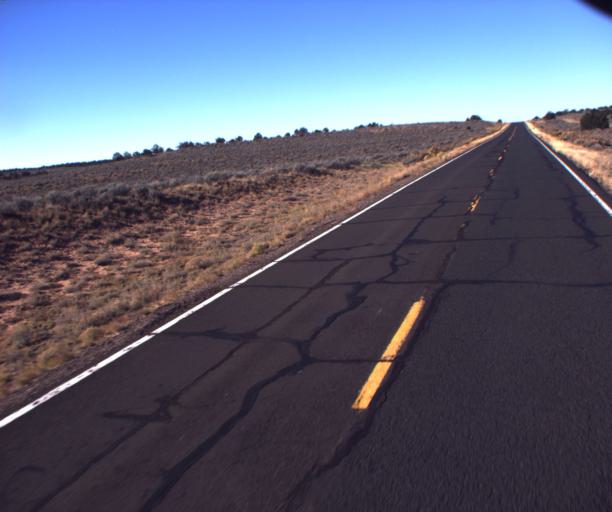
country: US
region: Arizona
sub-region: Navajo County
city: First Mesa
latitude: 35.7426
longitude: -110.0679
